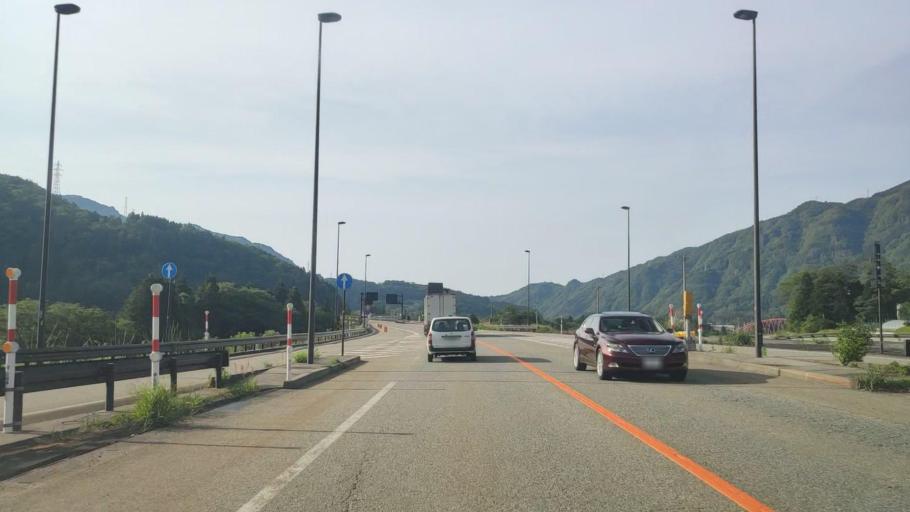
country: JP
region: Toyama
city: Yatsuomachi-higashikumisaka
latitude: 36.5234
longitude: 137.2310
